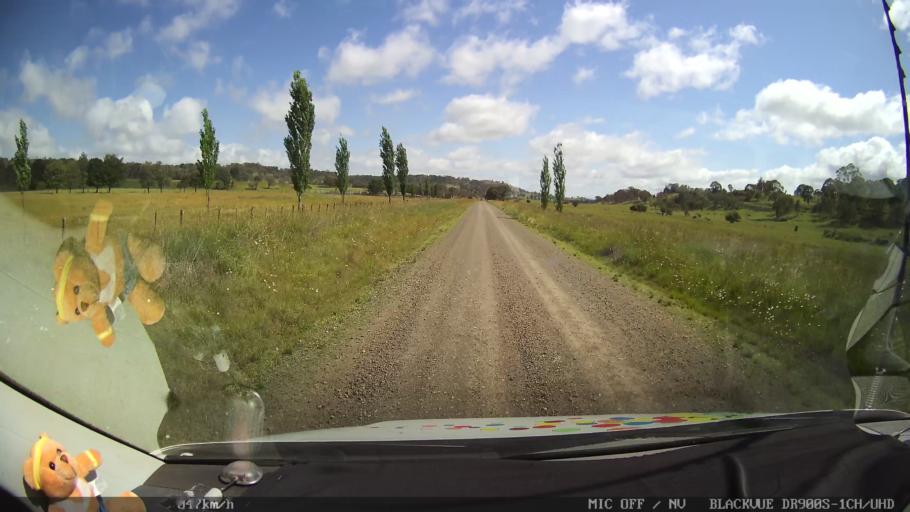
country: AU
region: New South Wales
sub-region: Glen Innes Severn
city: Glen Innes
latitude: -29.9725
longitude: 151.6992
